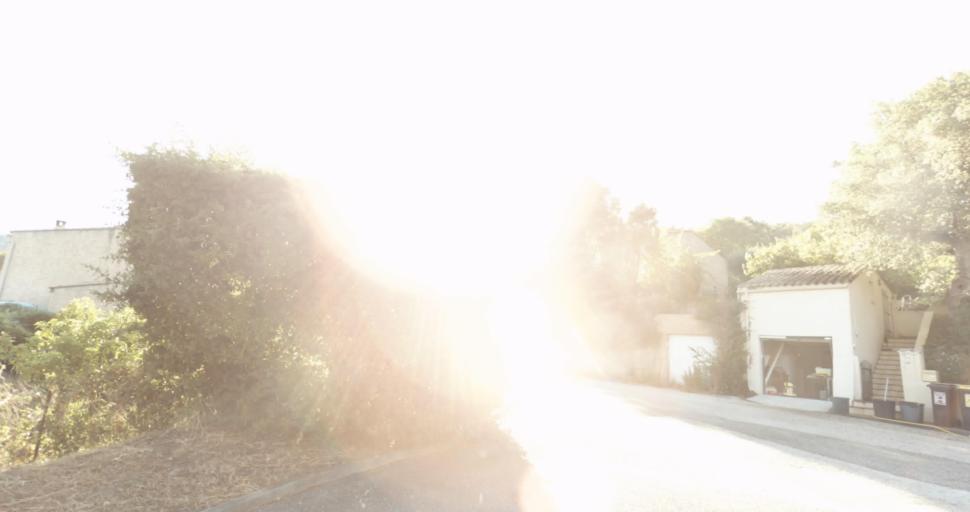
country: FR
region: Provence-Alpes-Cote d'Azur
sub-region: Departement du Var
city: La Croix-Valmer
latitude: 43.2247
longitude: 6.5662
